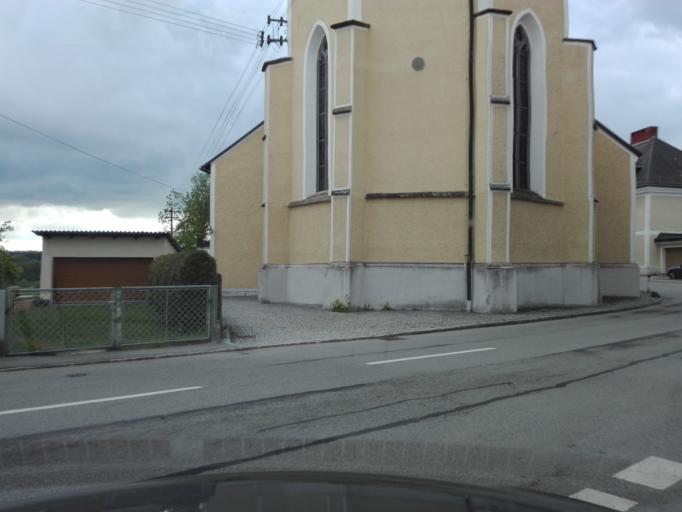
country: DE
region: Bavaria
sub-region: Lower Bavaria
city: Obernzell
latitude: 48.4818
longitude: 13.6117
